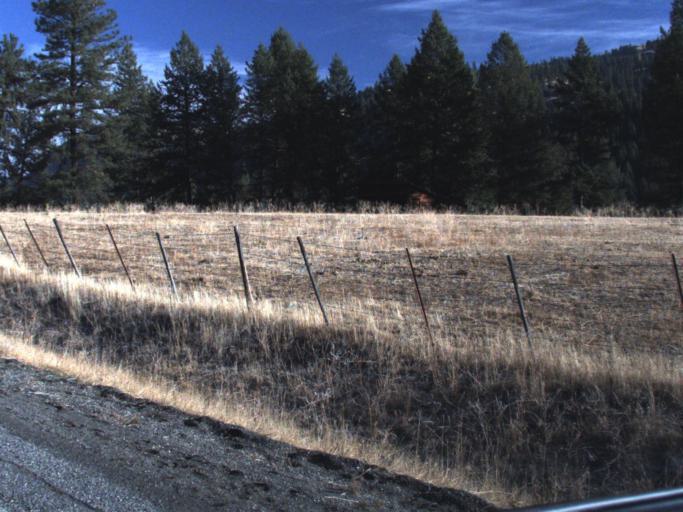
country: US
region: Washington
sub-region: Ferry County
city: Republic
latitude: 48.5845
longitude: -118.7424
